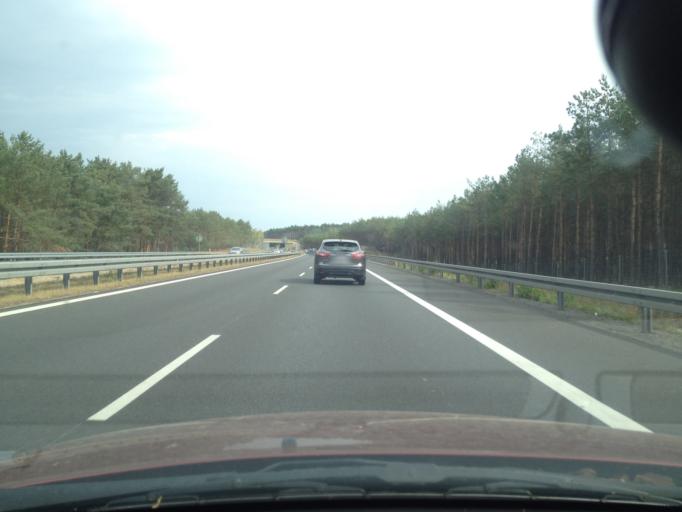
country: PL
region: Lubusz
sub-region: Zielona Gora
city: Zielona Gora
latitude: 51.9634
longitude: 15.5620
